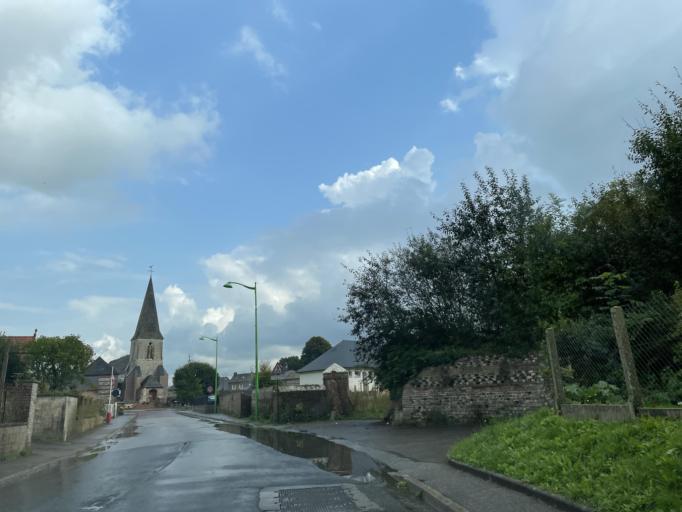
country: FR
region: Haute-Normandie
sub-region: Departement de la Seine-Maritime
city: Saint-Martin-en-Campagne
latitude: 49.9433
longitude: 1.2606
